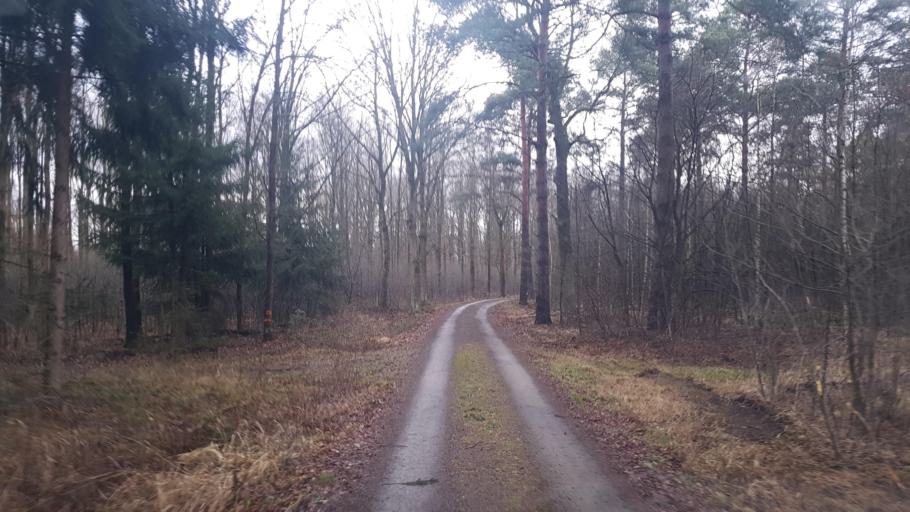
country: DE
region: Brandenburg
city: Schraden
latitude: 51.4441
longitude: 13.6696
